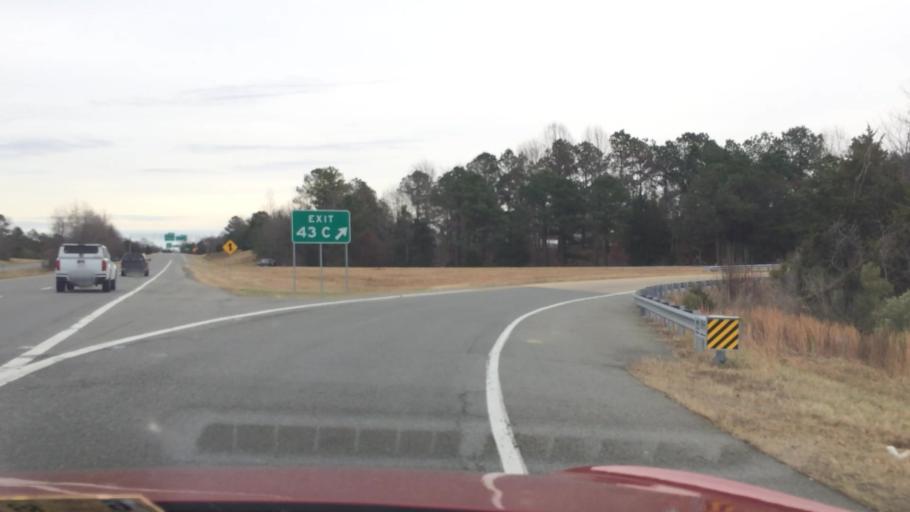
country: US
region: Virginia
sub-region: Henrico County
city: Chamberlayne
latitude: 37.6580
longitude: -77.4590
